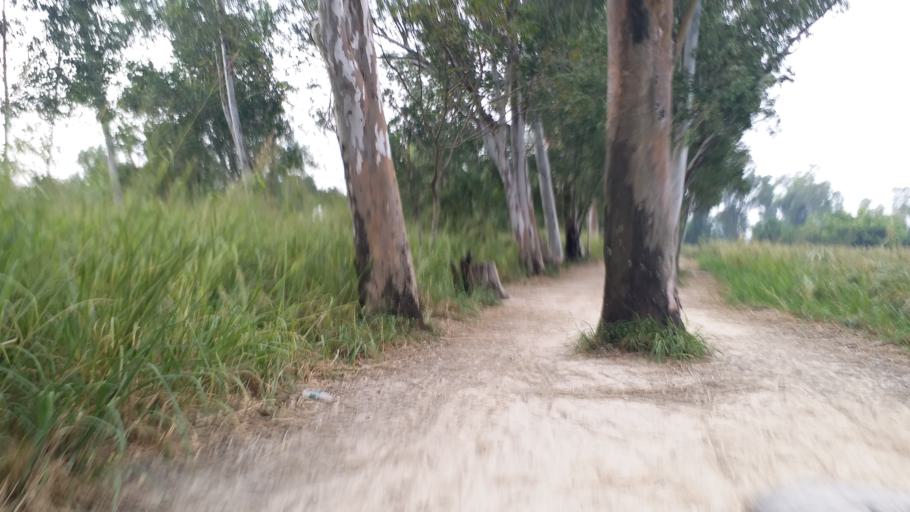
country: HK
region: Yuen Long
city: Yuen Long Kau Hui
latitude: 22.4574
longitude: 114.0343
